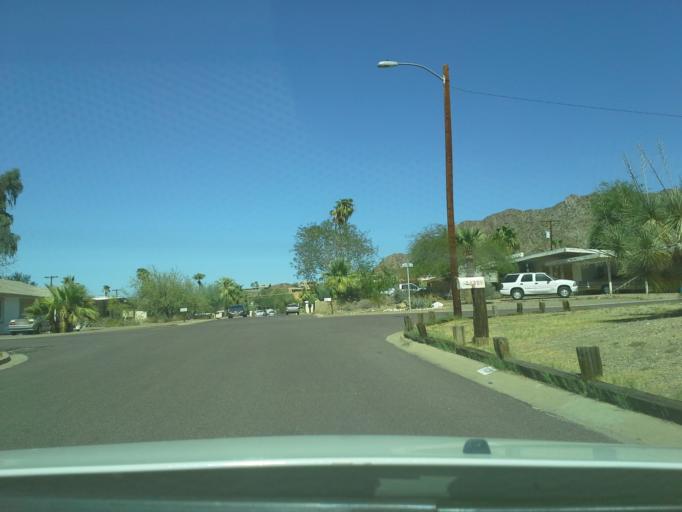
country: US
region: Arizona
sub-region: Maricopa County
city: Paradise Valley
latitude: 33.5727
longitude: -112.0471
